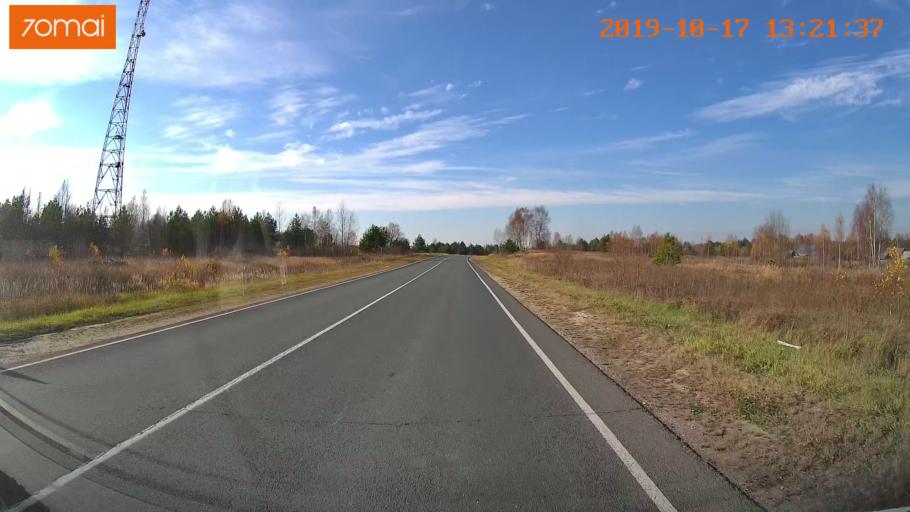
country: RU
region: Rjazan
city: Gus'-Zheleznyy
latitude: 55.0817
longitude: 41.0226
